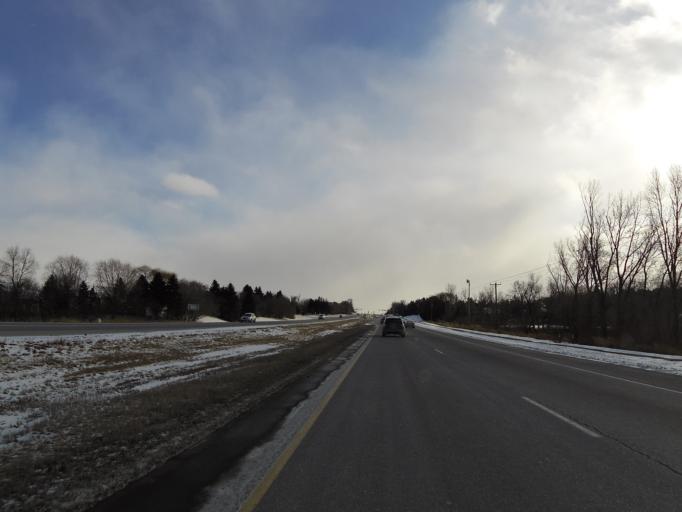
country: US
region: Minnesota
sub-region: Washington County
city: Woodbury
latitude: 44.9342
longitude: -92.9341
